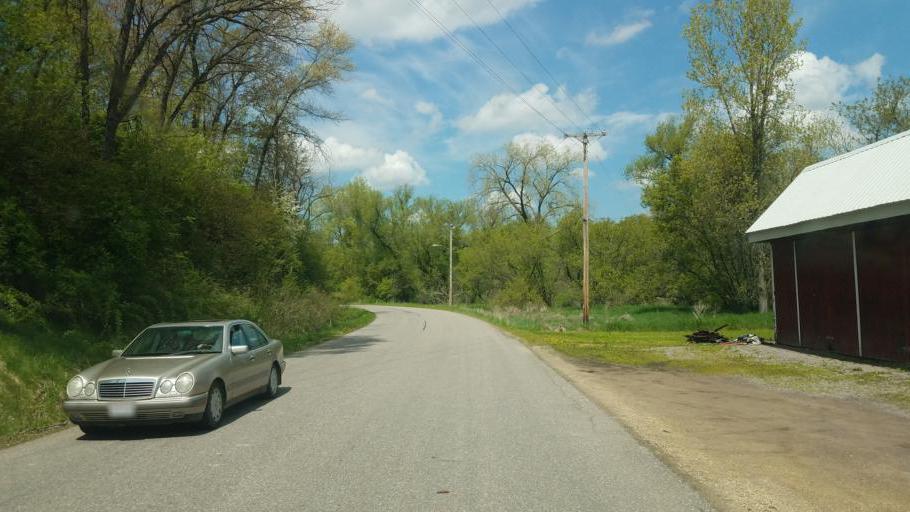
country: US
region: Wisconsin
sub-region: Vernon County
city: Hillsboro
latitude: 43.6495
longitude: -90.3342
